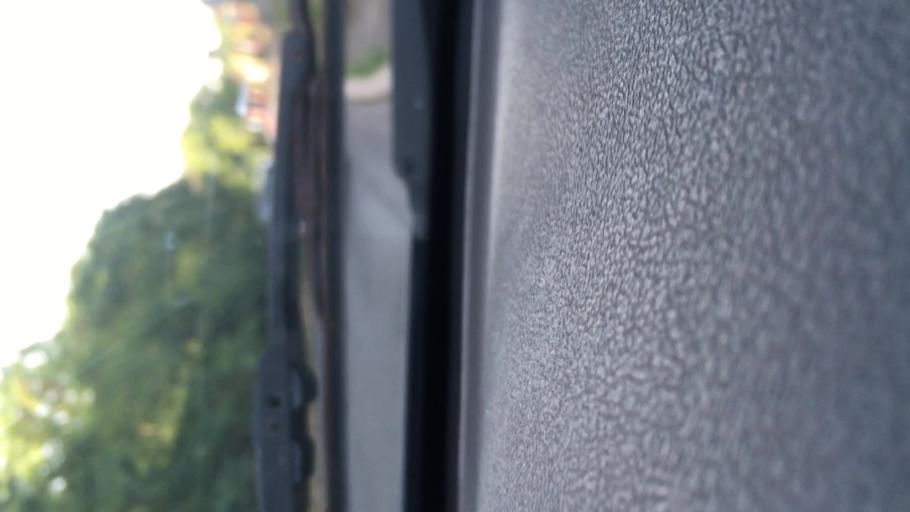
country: IT
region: Latium
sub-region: Citta metropolitana di Roma Capitale
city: Borgo Lotti
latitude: 41.8132
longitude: 12.5252
